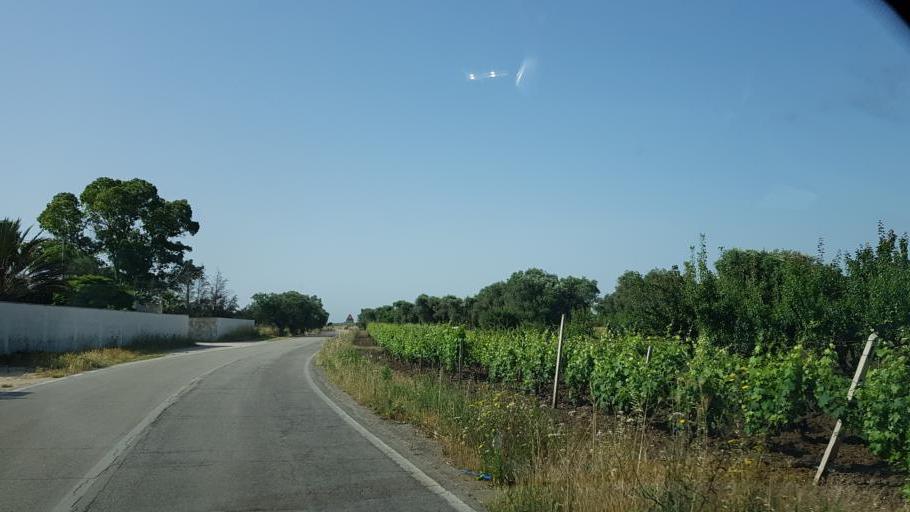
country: IT
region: Apulia
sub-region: Provincia di Brindisi
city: Mesagne
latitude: 40.5331
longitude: 17.8191
